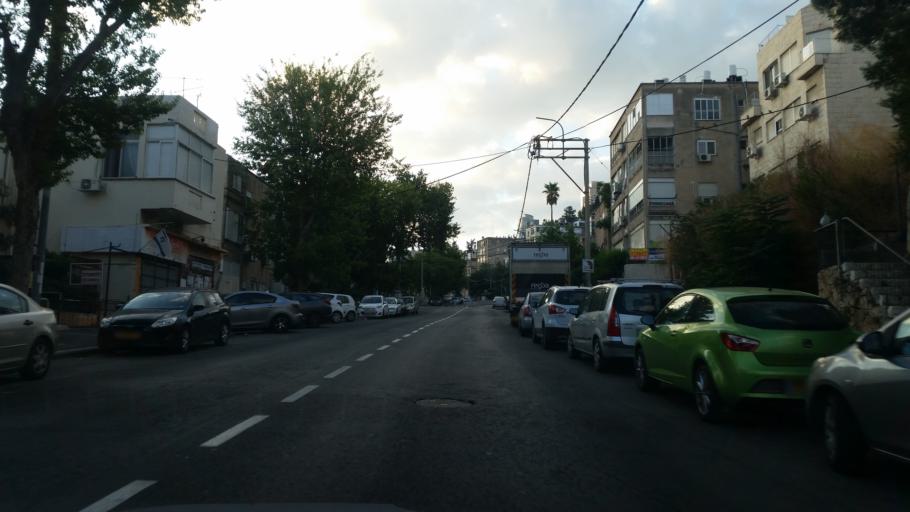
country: IL
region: Haifa
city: Haifa
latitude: 32.8008
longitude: 35.0113
